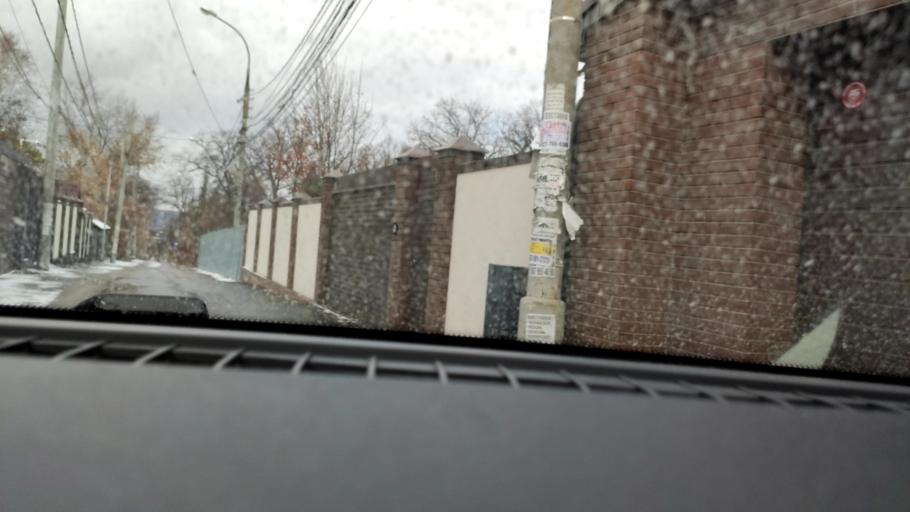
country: RU
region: Samara
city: Samara
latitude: 53.2729
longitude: 50.1996
